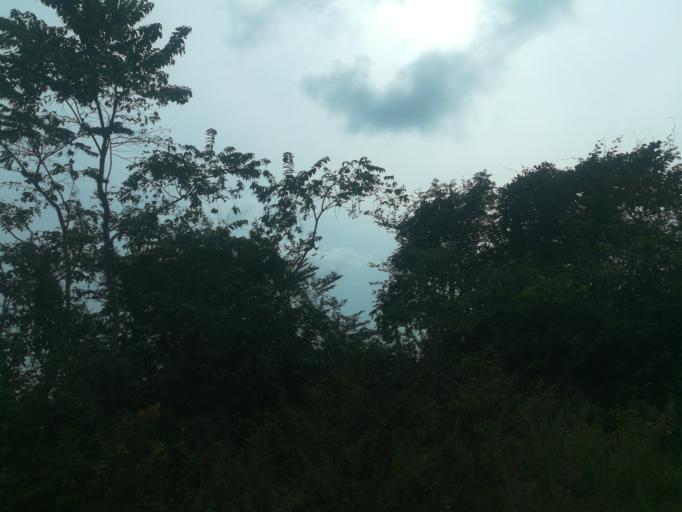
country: NG
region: Ogun
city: Ayetoro
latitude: 7.2748
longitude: 3.0987
